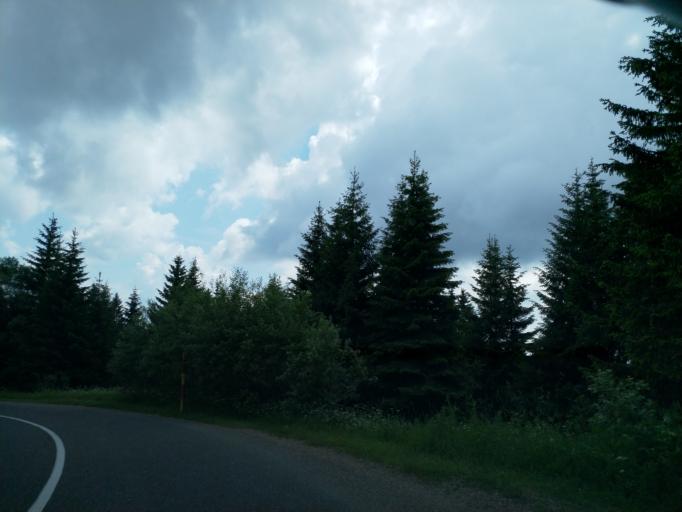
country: RS
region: Central Serbia
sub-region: Raski Okrug
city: Raska
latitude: 43.2828
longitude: 20.7933
